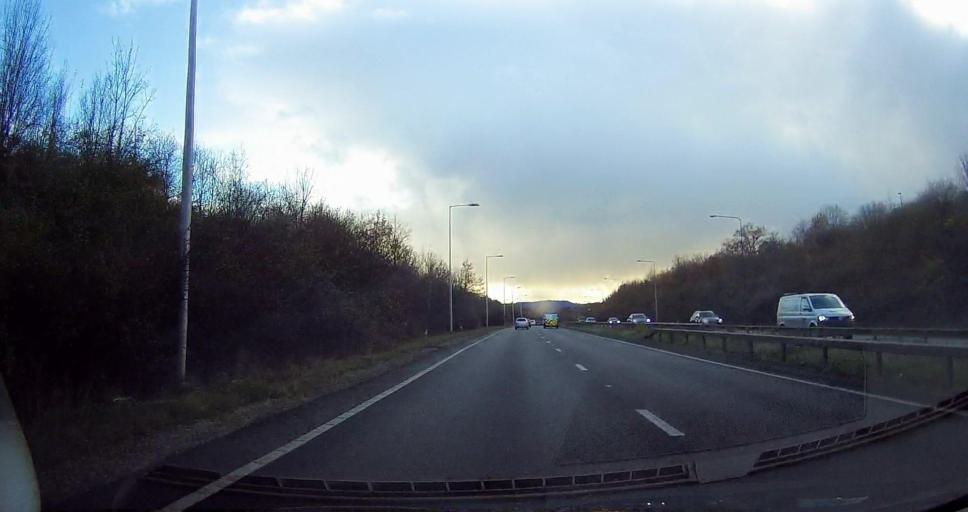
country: GB
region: England
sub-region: West Sussex
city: Hurstpierpoint
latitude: 50.9678
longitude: -0.1936
